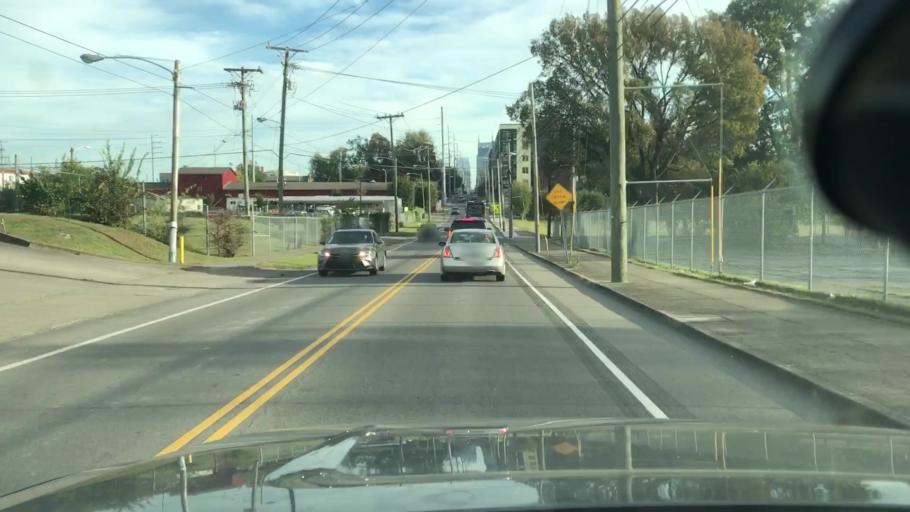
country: US
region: Tennessee
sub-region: Davidson County
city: Nashville
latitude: 36.1827
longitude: -86.7897
